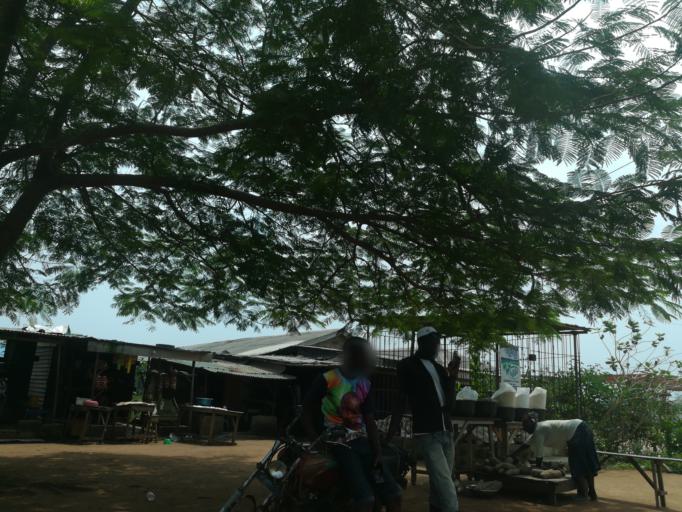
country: NG
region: Lagos
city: Ikorodu
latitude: 6.6035
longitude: 3.6063
